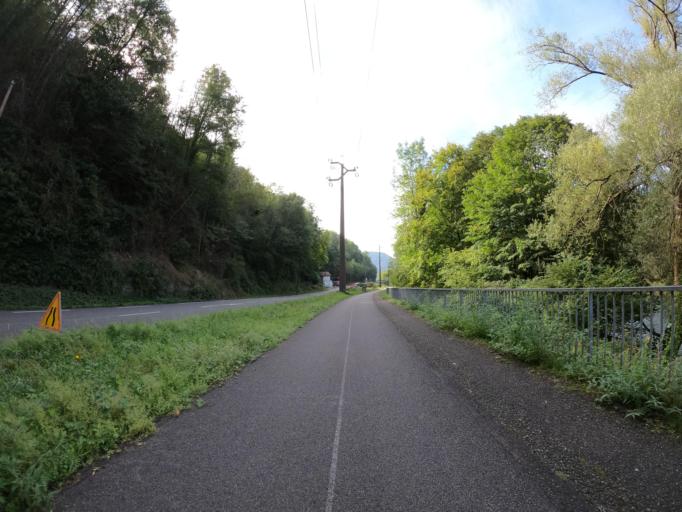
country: FR
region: Midi-Pyrenees
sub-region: Departement des Hautes-Pyrenees
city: Lourdes
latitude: 43.0728
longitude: -0.0401
